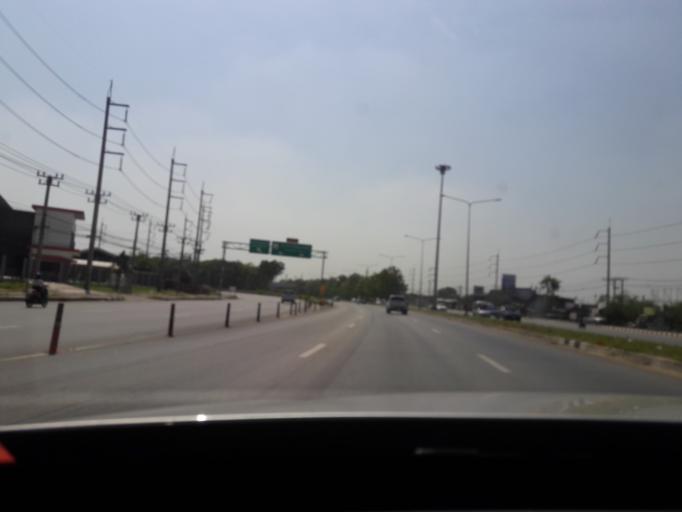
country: TH
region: Samut Sakhon
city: Krathum Baen
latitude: 13.6484
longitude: 100.3010
